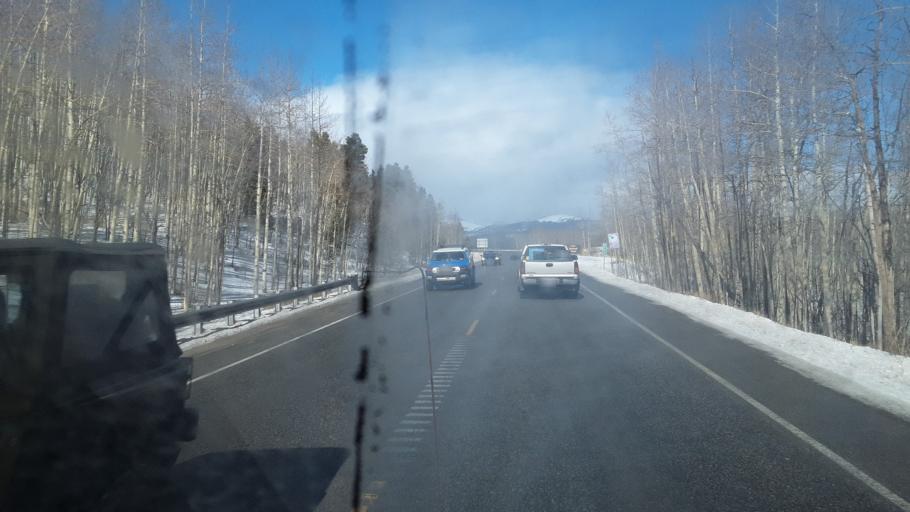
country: US
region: Colorado
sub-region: Summit County
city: Breckenridge
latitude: 39.4083
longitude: -105.7559
